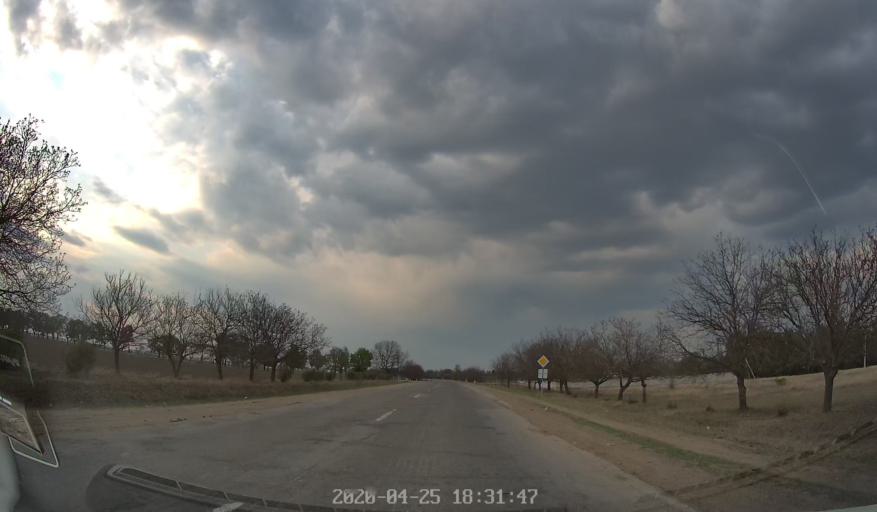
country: MD
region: Criuleni
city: Criuleni
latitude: 47.2218
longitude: 29.1459
